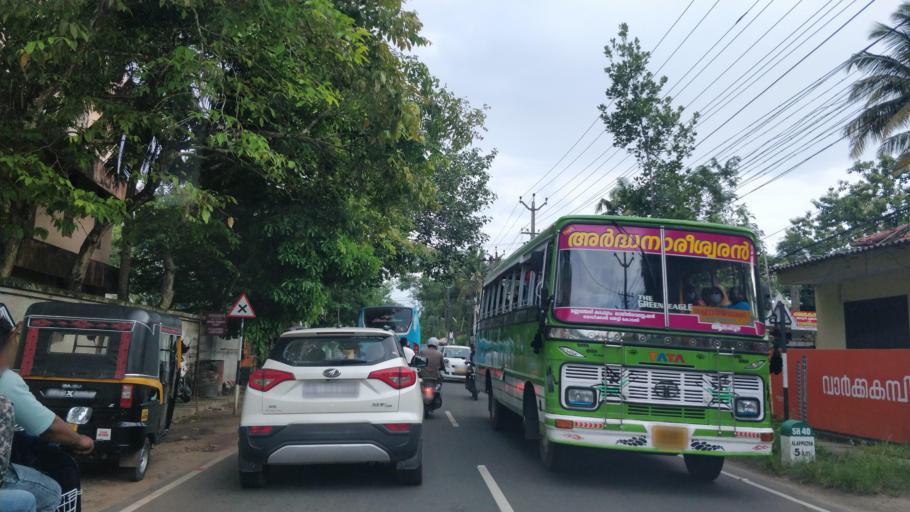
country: IN
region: Kerala
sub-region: Alappuzha
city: Alleppey
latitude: 9.5316
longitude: 76.3412
